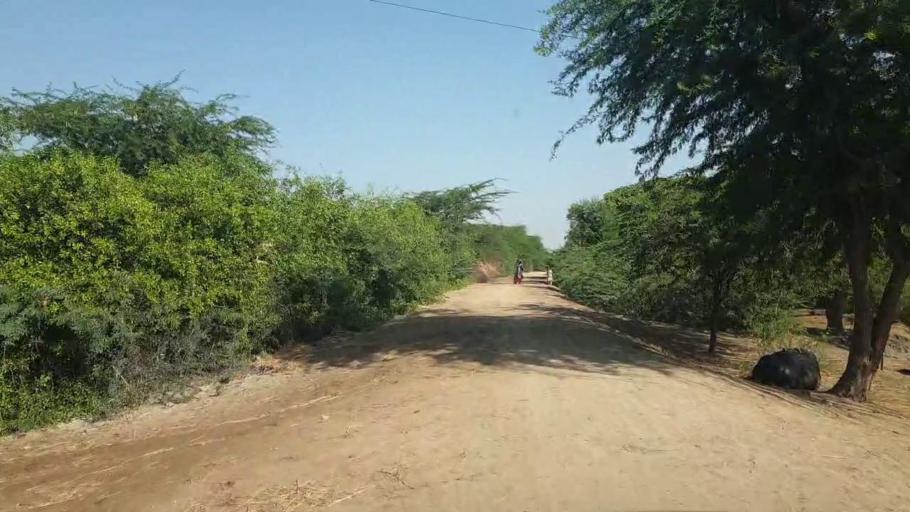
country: PK
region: Sindh
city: Talhar
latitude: 24.7779
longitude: 68.8058
